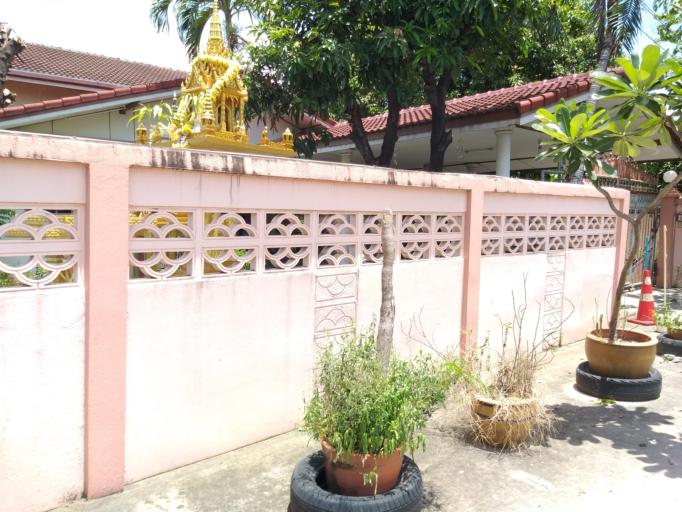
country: TH
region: Bangkok
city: Lat Phrao
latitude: 13.8257
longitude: 100.6256
